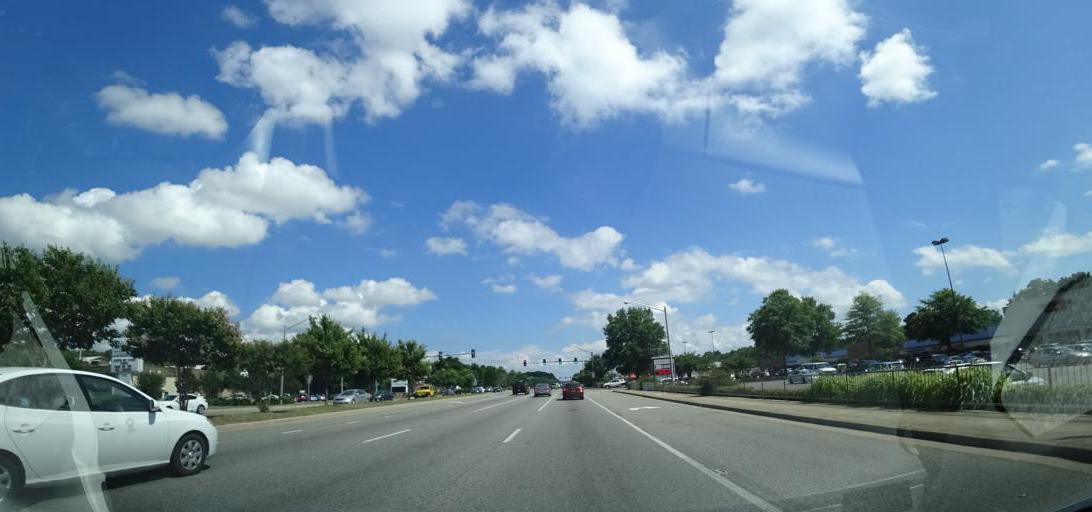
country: US
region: Virginia
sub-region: York County
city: Yorktown
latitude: 37.1373
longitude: -76.5191
